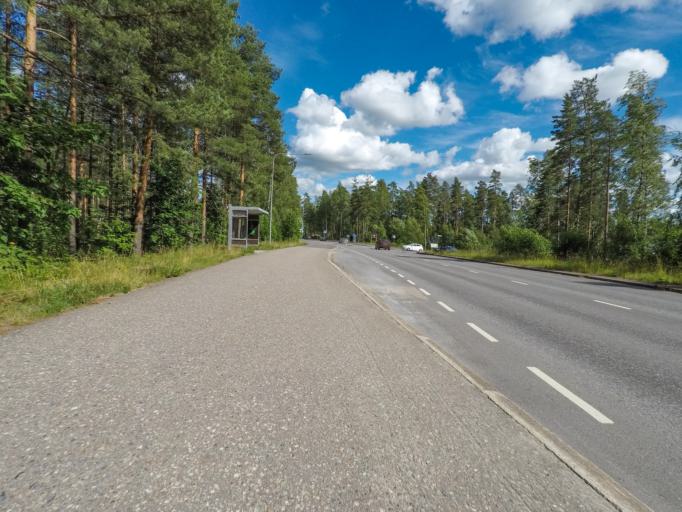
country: FI
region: South Karelia
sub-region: Lappeenranta
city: Lappeenranta
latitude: 61.0783
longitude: 28.3024
